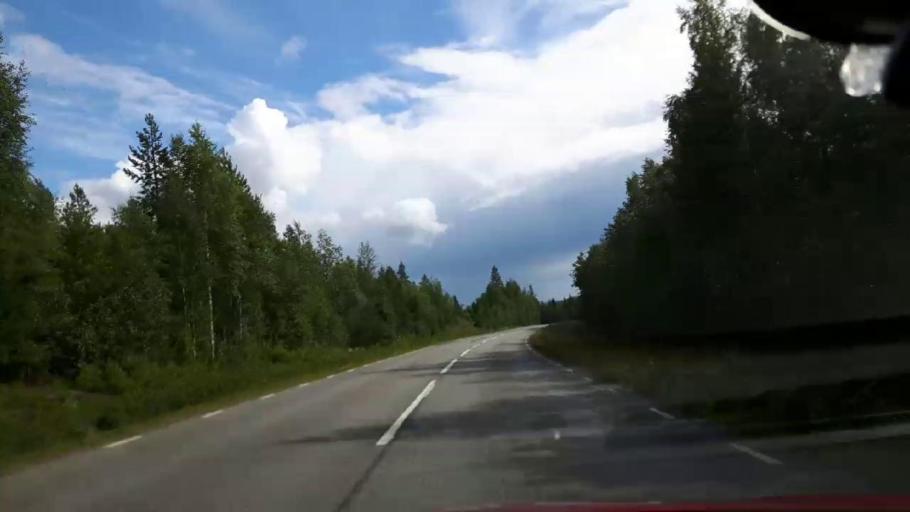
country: SE
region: Jaemtland
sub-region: Stroemsunds Kommun
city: Stroemsund
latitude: 64.3444
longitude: 15.1057
